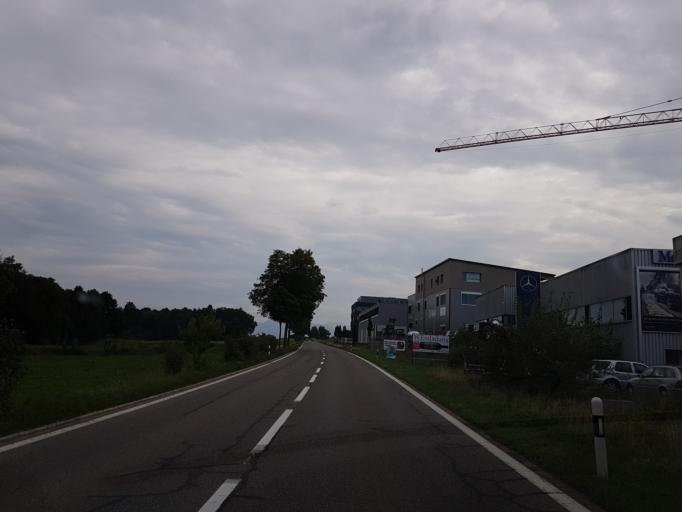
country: CH
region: Aargau
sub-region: Bezirk Muri
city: Muri
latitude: 47.2607
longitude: 8.3532
